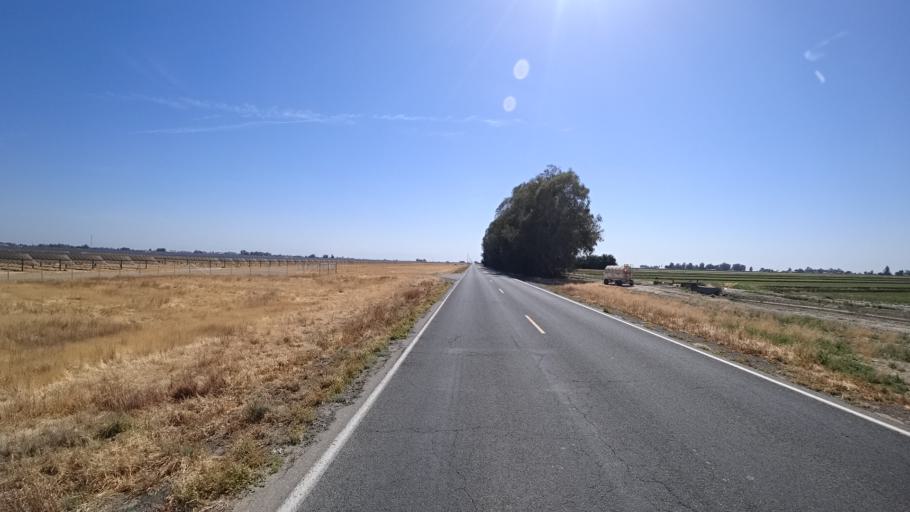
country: US
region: California
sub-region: Kings County
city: Stratford
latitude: 36.2115
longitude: -119.8076
